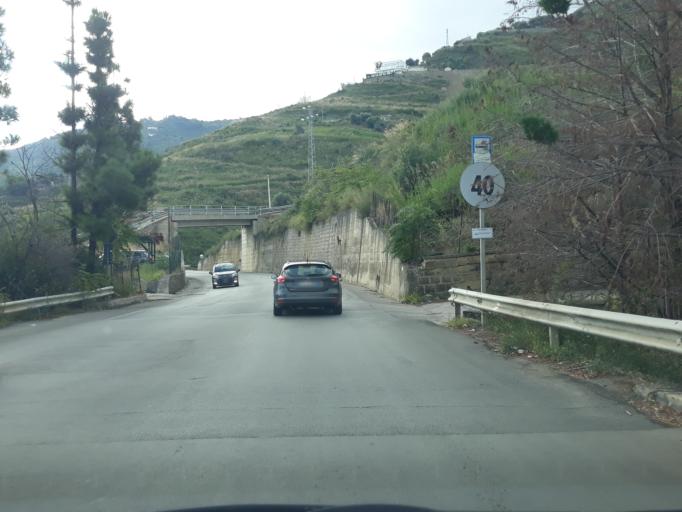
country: IT
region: Sicily
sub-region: Palermo
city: Cefalu
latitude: 38.0286
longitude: 14.0056
